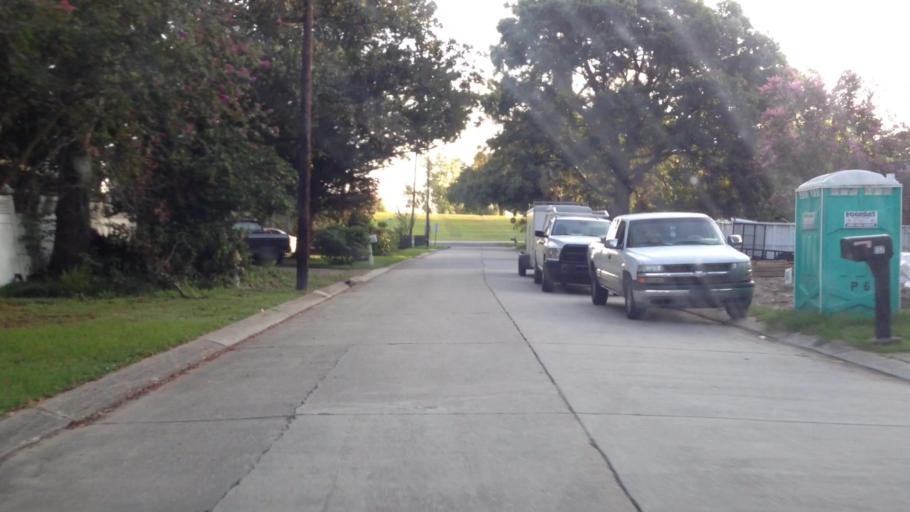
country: US
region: Louisiana
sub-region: Jefferson Parish
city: Jefferson
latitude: 29.9492
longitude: -90.1545
